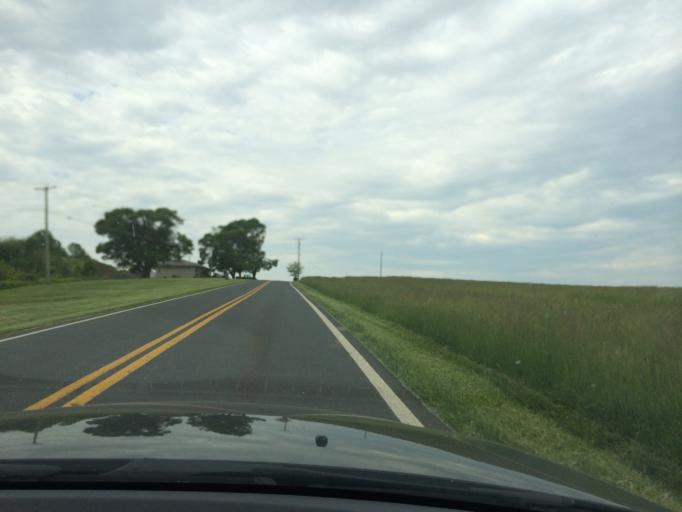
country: US
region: Maryland
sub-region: Carroll County
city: Eldersburg
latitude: 39.4360
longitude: -76.9737
